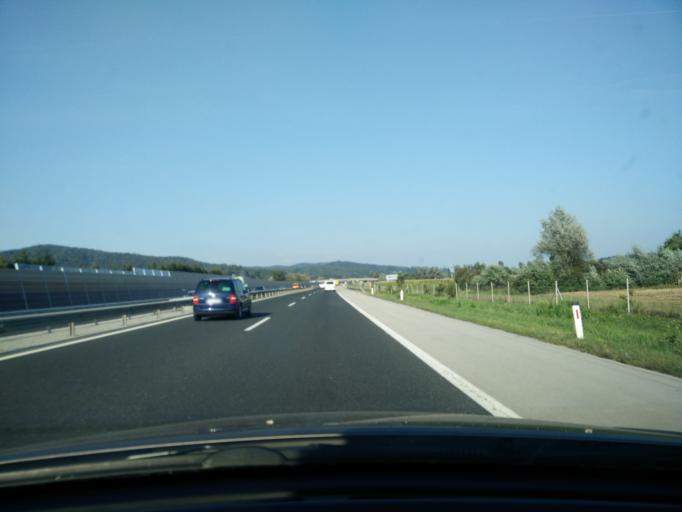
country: SI
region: Vrhnika
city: Verd
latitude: 45.9902
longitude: 14.3256
